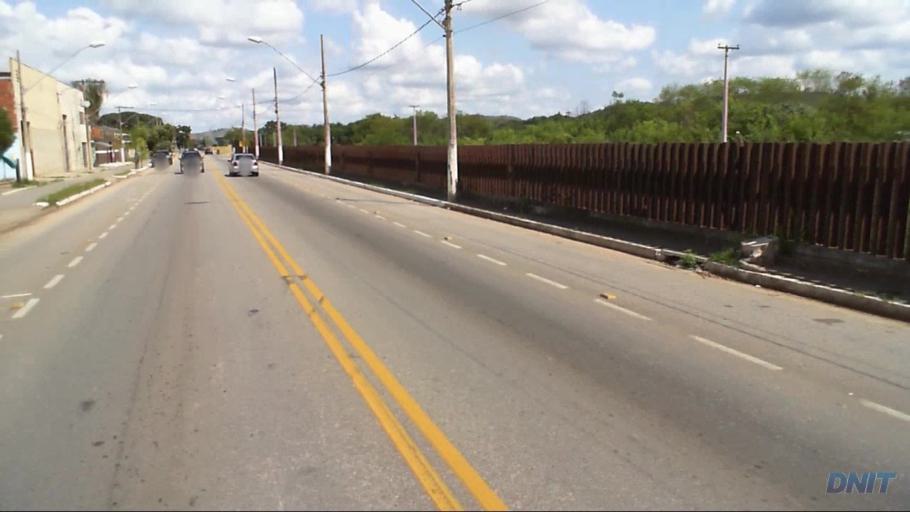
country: BR
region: Minas Gerais
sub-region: Governador Valadares
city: Governador Valadares
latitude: -18.9018
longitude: -41.9867
